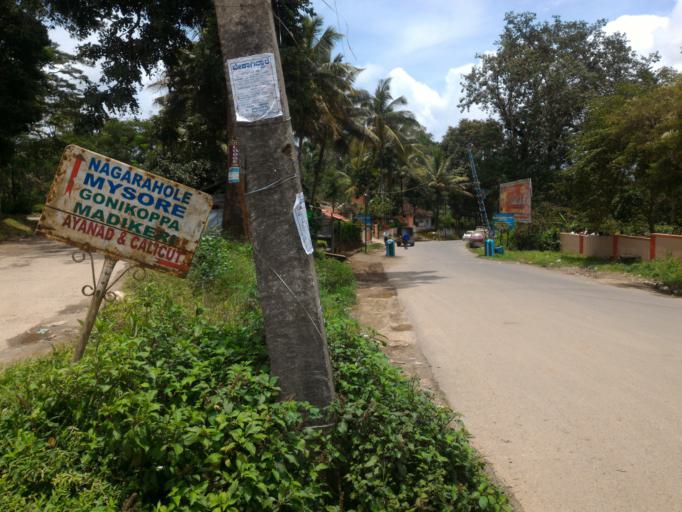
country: IN
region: Karnataka
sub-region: Kodagu
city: Ponnampet
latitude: 11.9690
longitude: 76.0511
